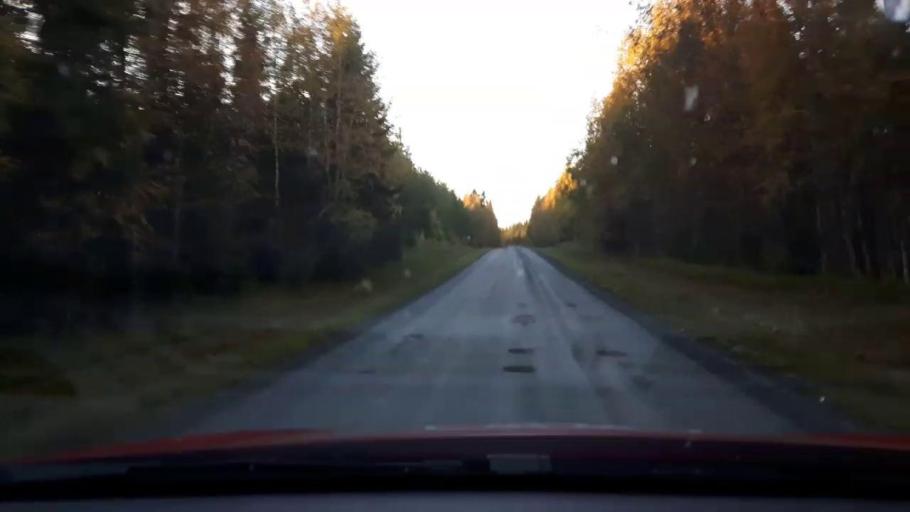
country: SE
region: Jaemtland
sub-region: Krokoms Kommun
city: Krokom
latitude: 63.4608
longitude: 14.3939
